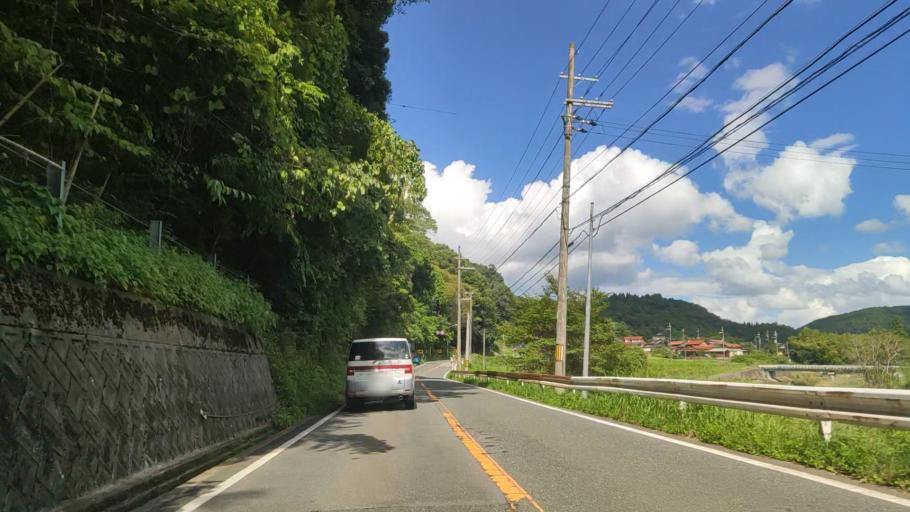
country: JP
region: Hyogo
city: Toyooka
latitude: 35.4941
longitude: 134.9593
